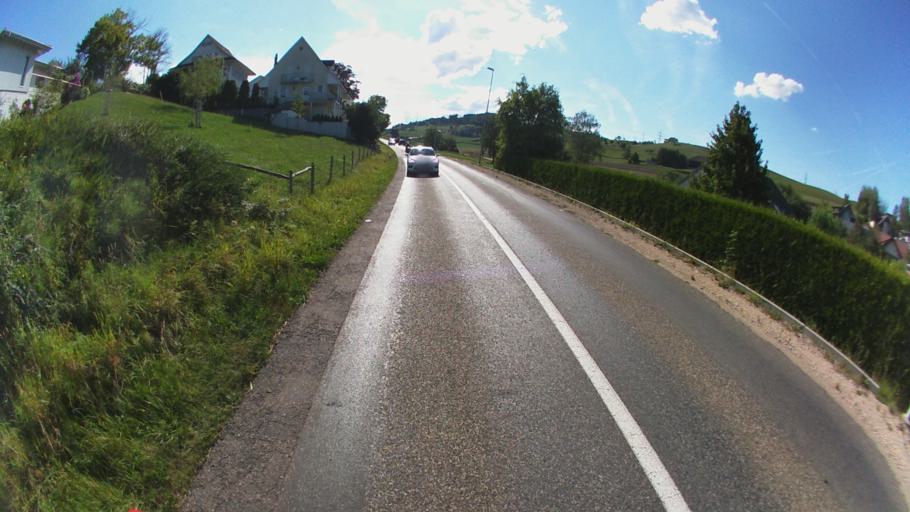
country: CH
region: Aargau
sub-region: Bezirk Rheinfelden
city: Wegenstetten
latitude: 47.4953
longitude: 7.9277
